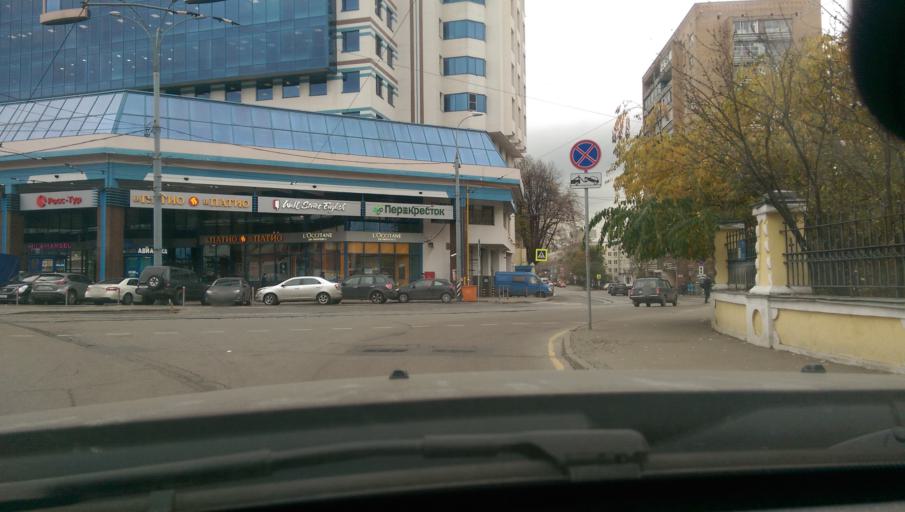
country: RU
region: Moscow
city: Mar'ina Roshcha
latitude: 55.7810
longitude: 37.6314
